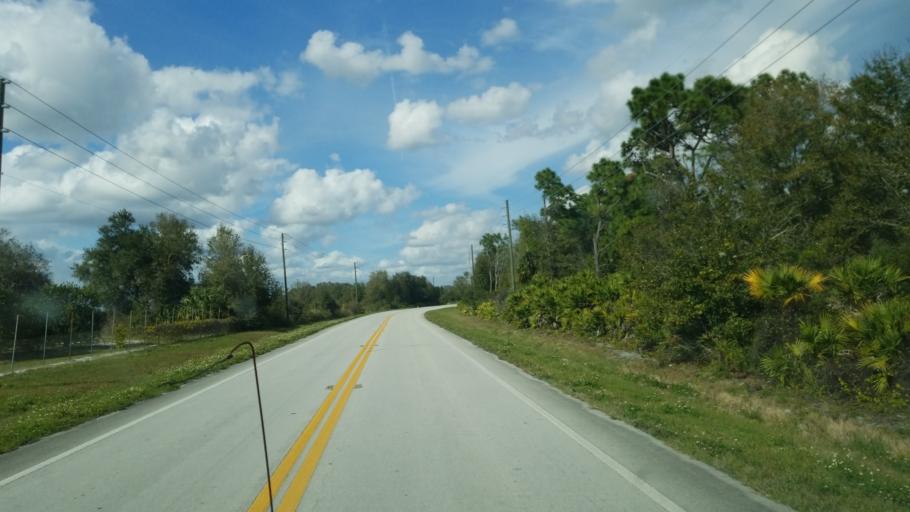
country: US
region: Florida
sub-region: Osceola County
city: Saint Cloud
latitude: 28.0967
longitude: -81.0758
